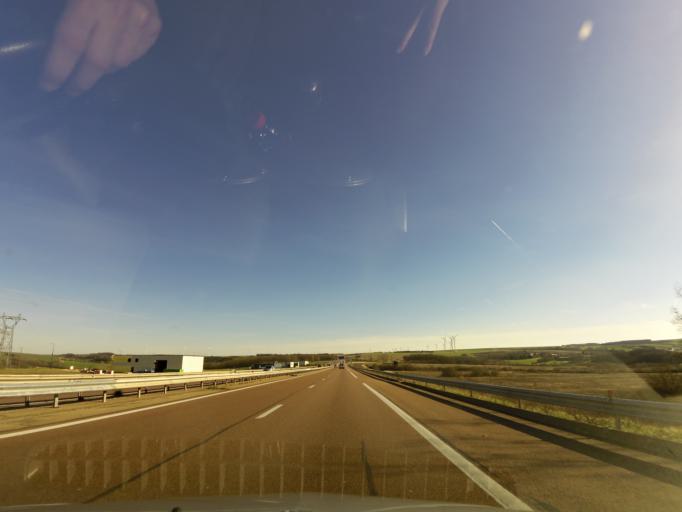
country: FR
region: Bourgogne
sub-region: Departement de l'Yonne
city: Venoy
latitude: 47.8018
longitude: 3.6414
